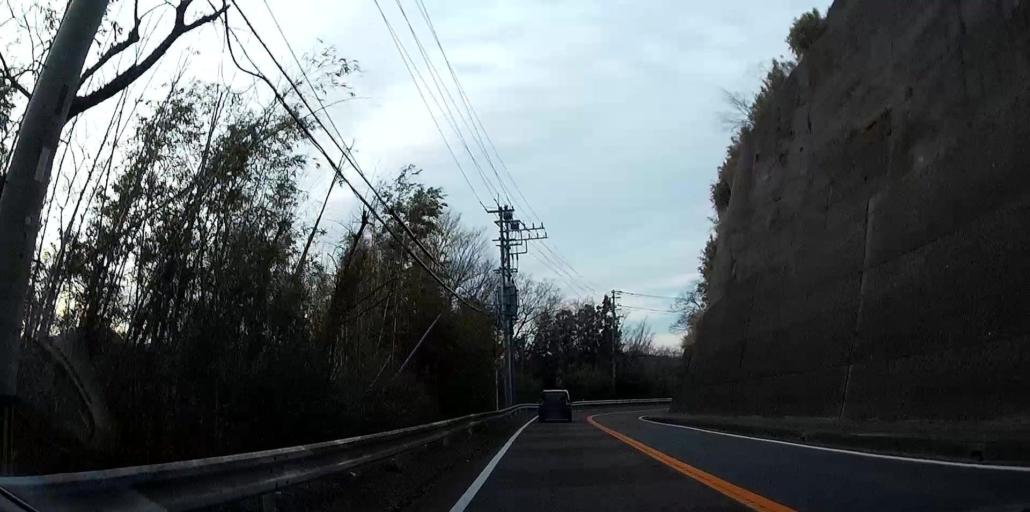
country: JP
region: Chiba
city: Kisarazu
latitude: 35.2711
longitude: 140.0640
